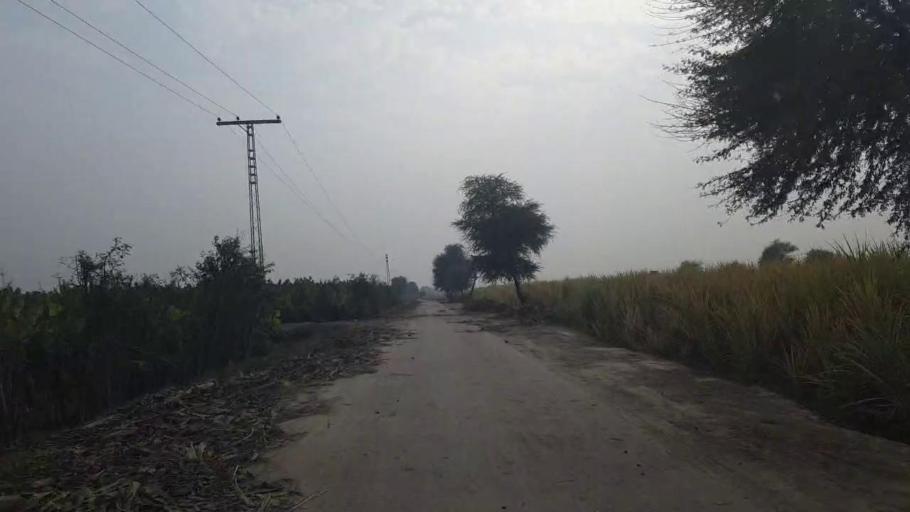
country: PK
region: Sindh
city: Berani
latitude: 25.8050
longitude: 68.7326
